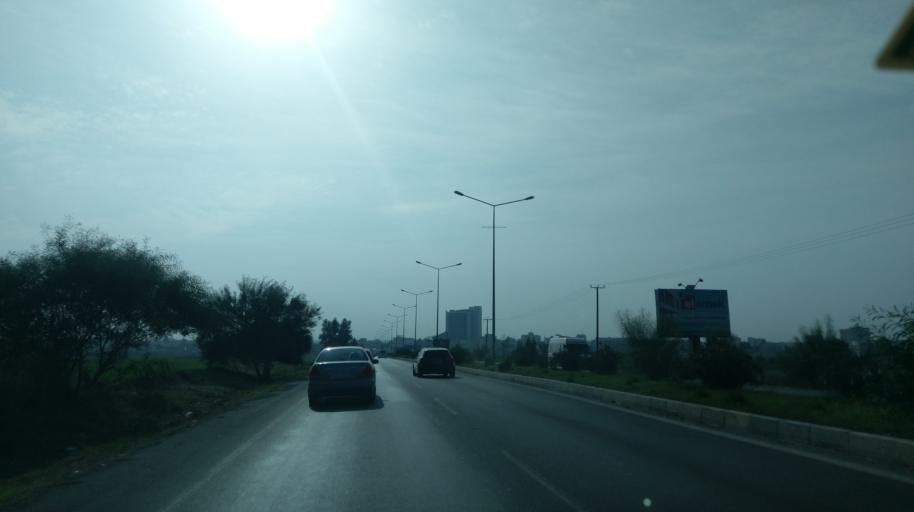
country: CY
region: Lefkosia
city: Nicosia
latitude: 35.2177
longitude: 33.3186
